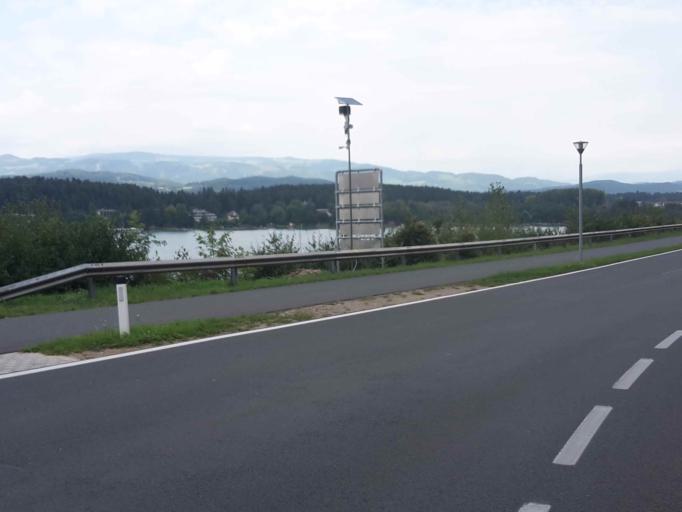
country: AT
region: Carinthia
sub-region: Politischer Bezirk Volkermarkt
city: Eberndorf
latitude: 46.6009
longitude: 14.5869
